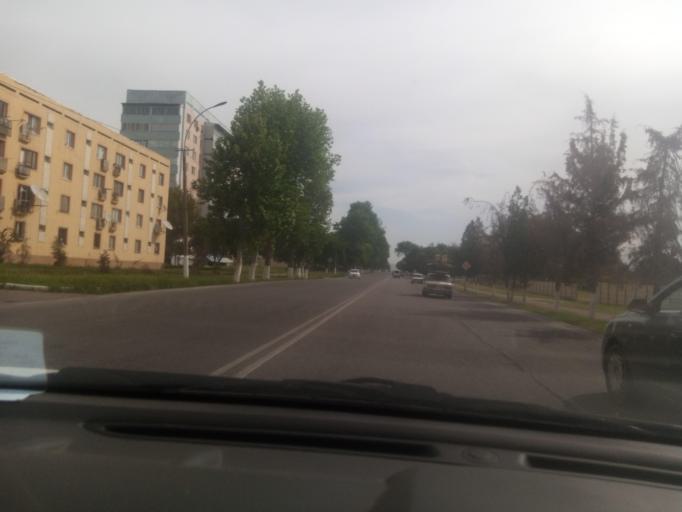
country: UZ
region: Toshkent
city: Angren
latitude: 40.9999
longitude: 70.0750
